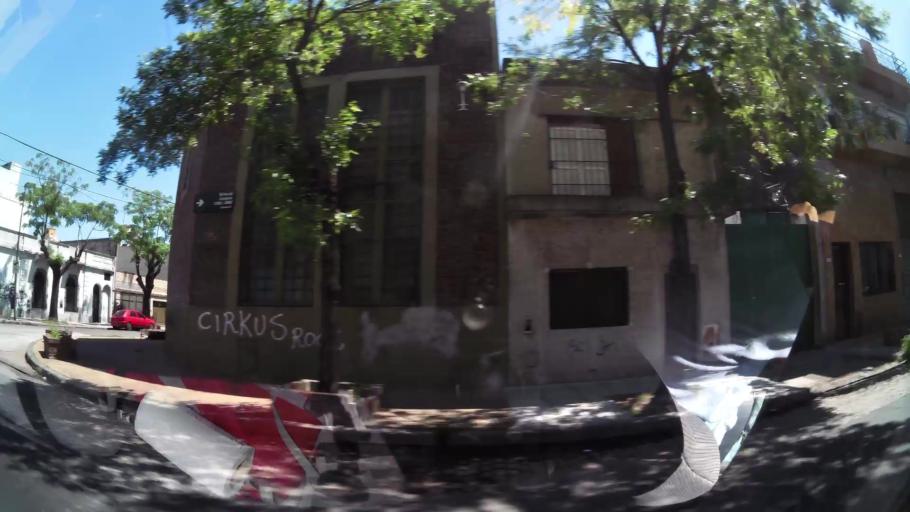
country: AR
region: Buenos Aires
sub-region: Partido de Avellaneda
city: Avellaneda
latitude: -34.6480
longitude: -58.4134
